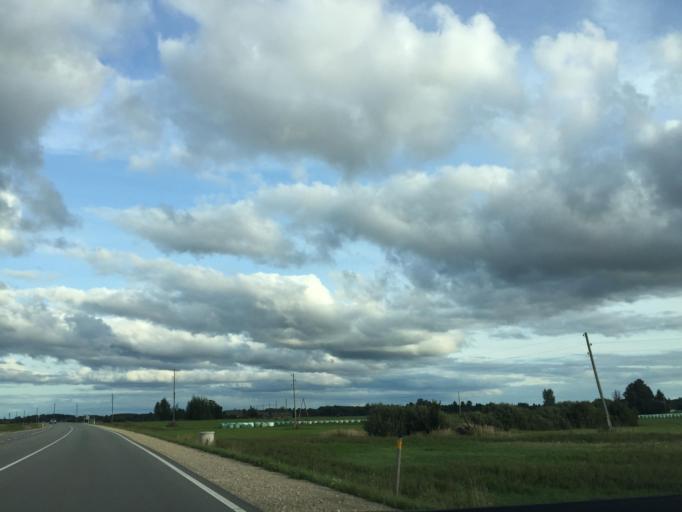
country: LV
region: Nereta
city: Nereta
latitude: 56.2518
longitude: 25.2187
